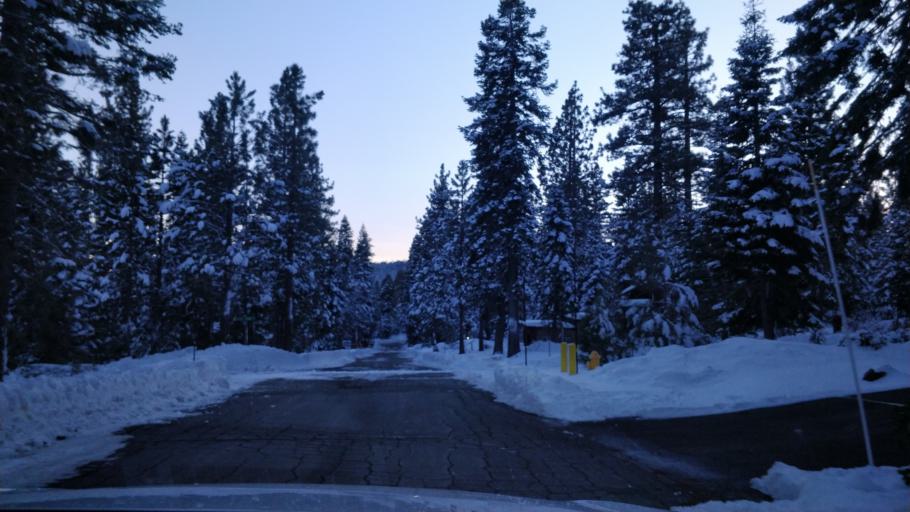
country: US
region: California
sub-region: Placer County
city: Sunnyside-Tahoe City
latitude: 39.1477
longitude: -120.1669
